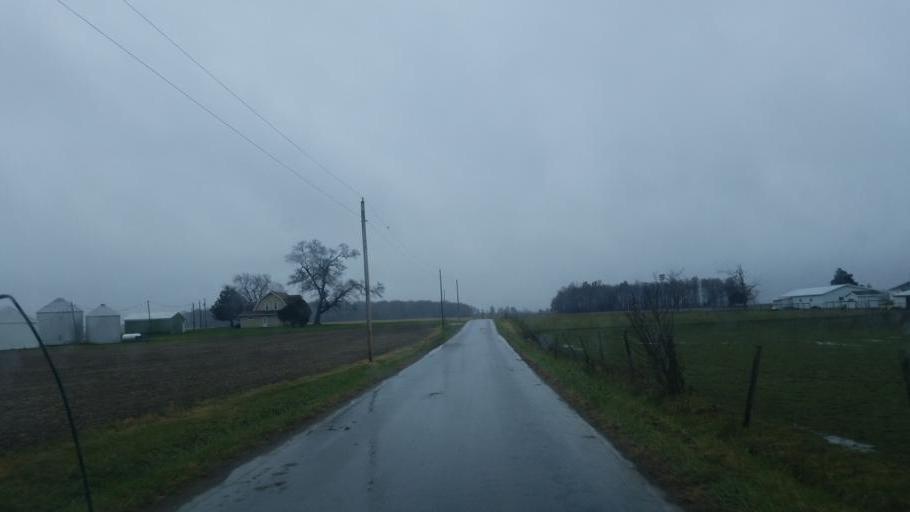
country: US
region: Indiana
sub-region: Adams County
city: Geneva
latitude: 40.6168
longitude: -84.8784
